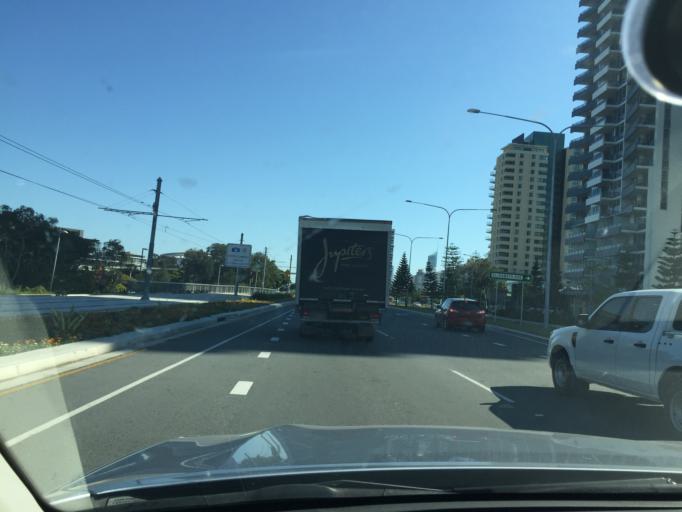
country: AU
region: Queensland
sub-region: Gold Coast
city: Surfers Paradise
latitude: -28.0327
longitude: 153.4307
